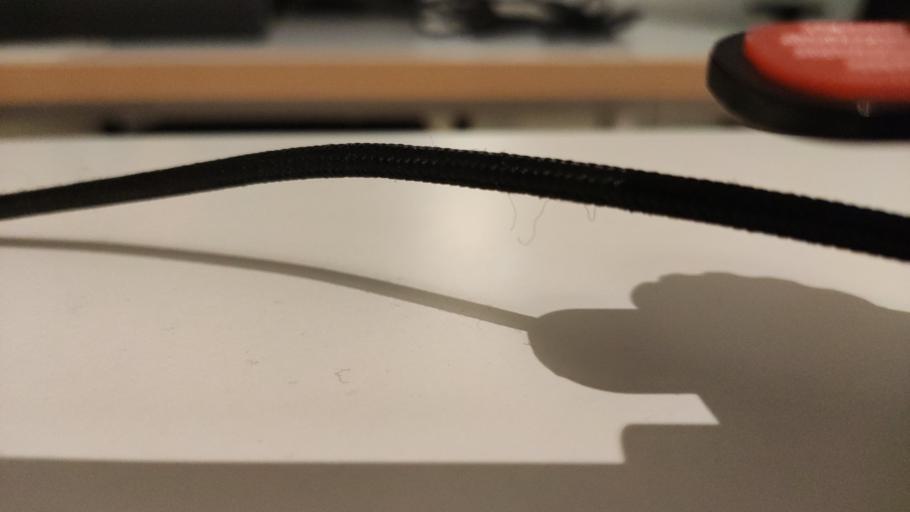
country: RU
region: Moskovskaya
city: Novosin'kovo
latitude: 56.3728
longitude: 37.3402
